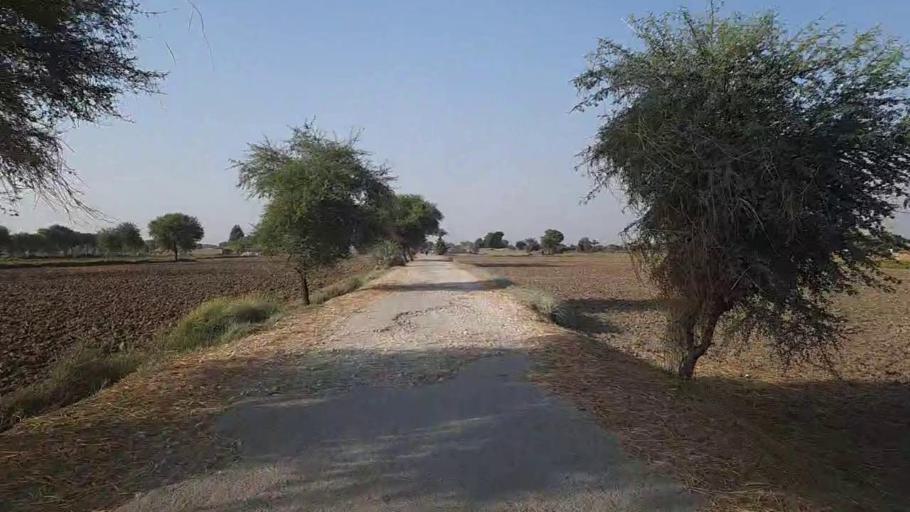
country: PK
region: Sindh
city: Kashmor
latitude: 28.4111
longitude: 69.4120
